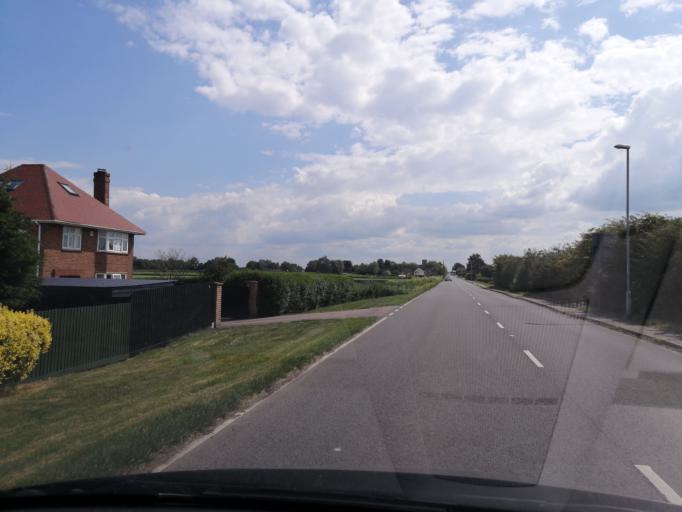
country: GB
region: England
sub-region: Cambridgeshire
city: Ramsey
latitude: 52.4744
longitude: -0.1525
